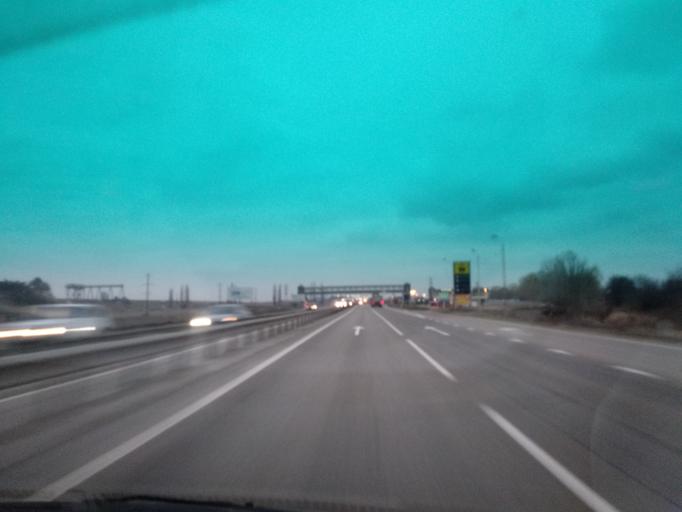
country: RU
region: Adygeya
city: Adygeysk
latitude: 44.9150
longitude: 39.1497
